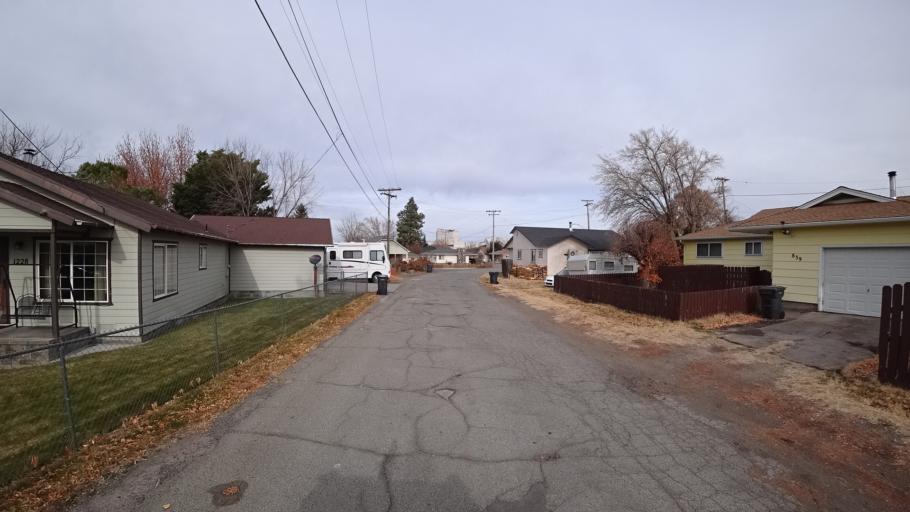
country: US
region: California
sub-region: Siskiyou County
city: Weed
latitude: 41.4312
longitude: -122.3768
